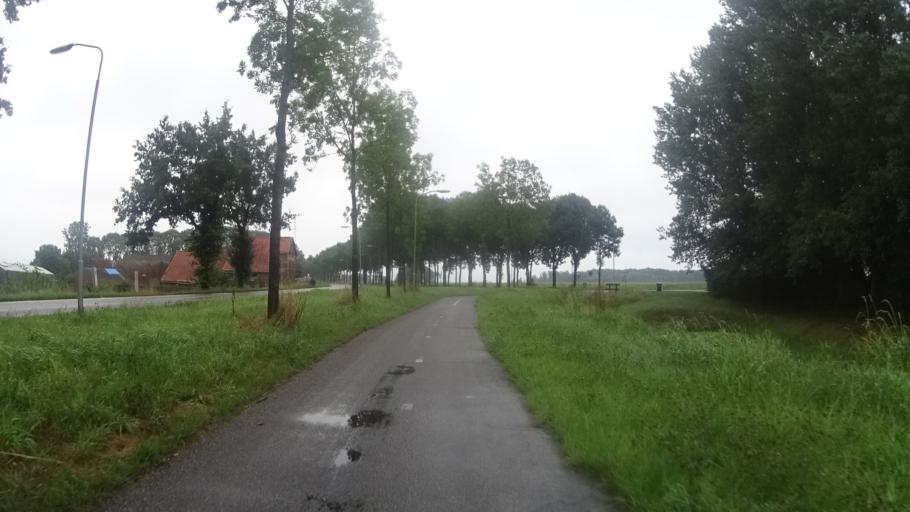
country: NL
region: Groningen
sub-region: Gemeente  Oldambt
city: Winschoten
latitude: 53.1548
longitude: 7.0725
